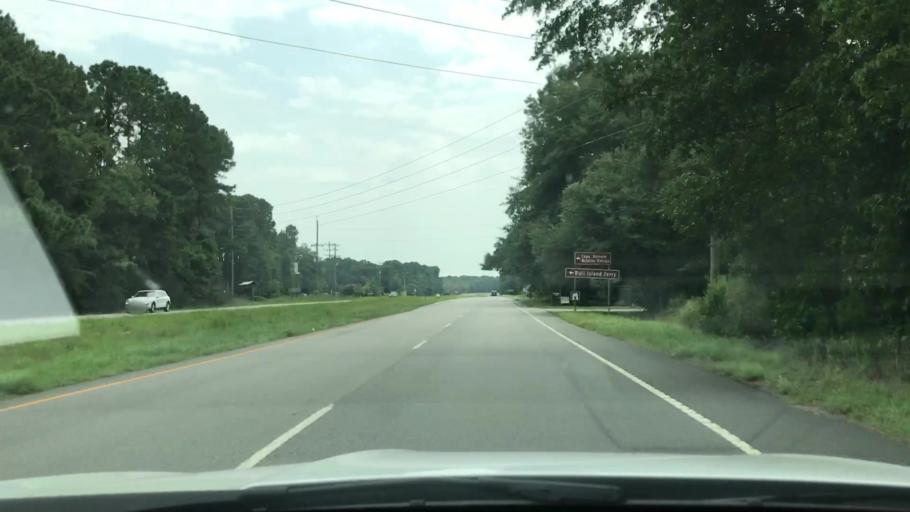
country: US
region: South Carolina
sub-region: Charleston County
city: Awendaw
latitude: 32.9282
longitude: -79.7142
